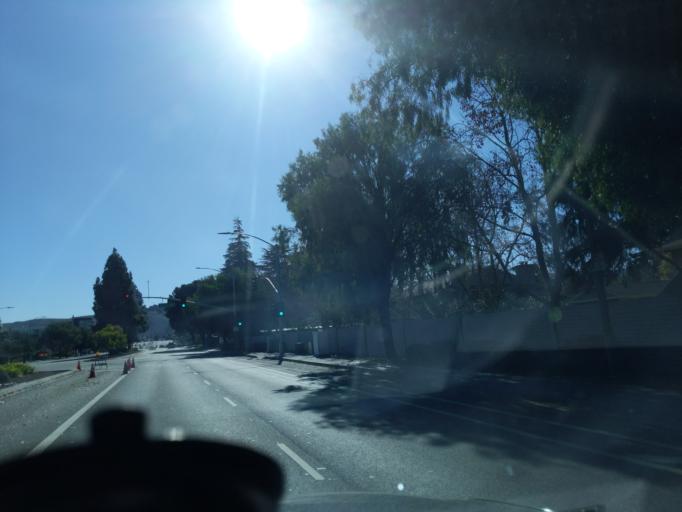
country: US
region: California
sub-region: Santa Clara County
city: Seven Trees
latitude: 37.2490
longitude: -121.8041
